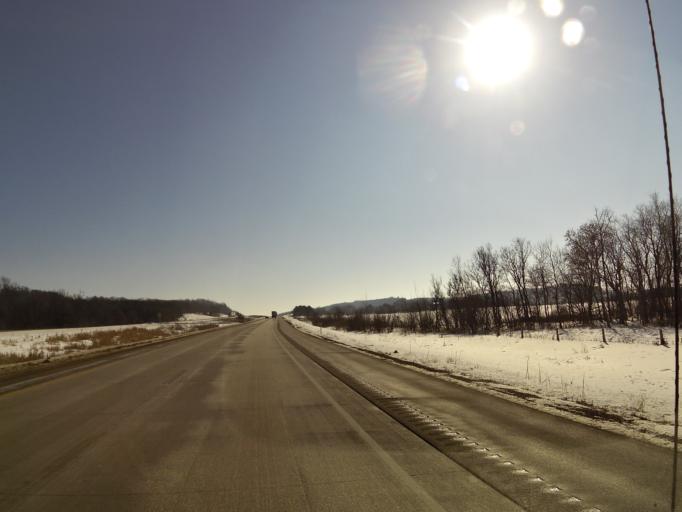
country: US
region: Wisconsin
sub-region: Trempealeau County
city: Osseo
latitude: 44.6184
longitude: -91.2506
